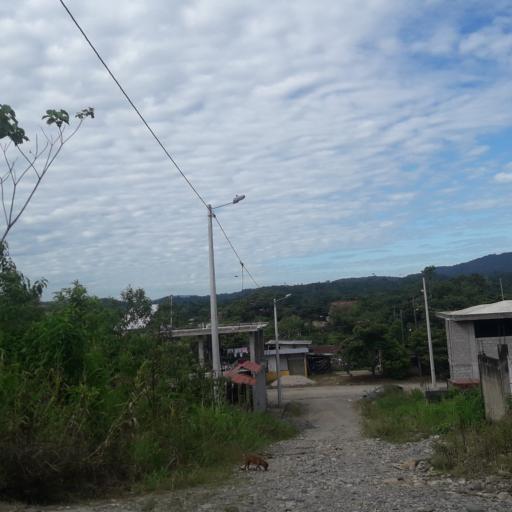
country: EC
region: Napo
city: Tena
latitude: -0.9824
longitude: -77.8260
